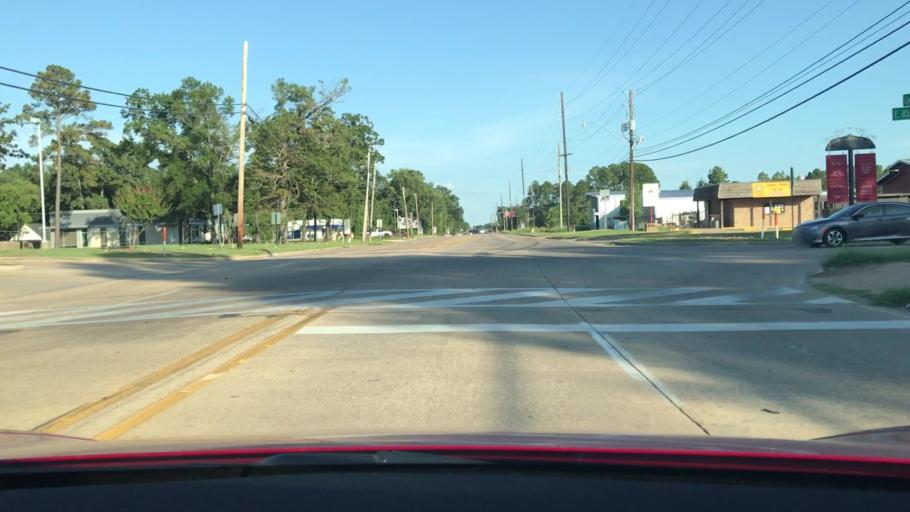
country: US
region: Louisiana
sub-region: Bossier Parish
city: Bossier City
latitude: 32.4286
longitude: -93.7430
